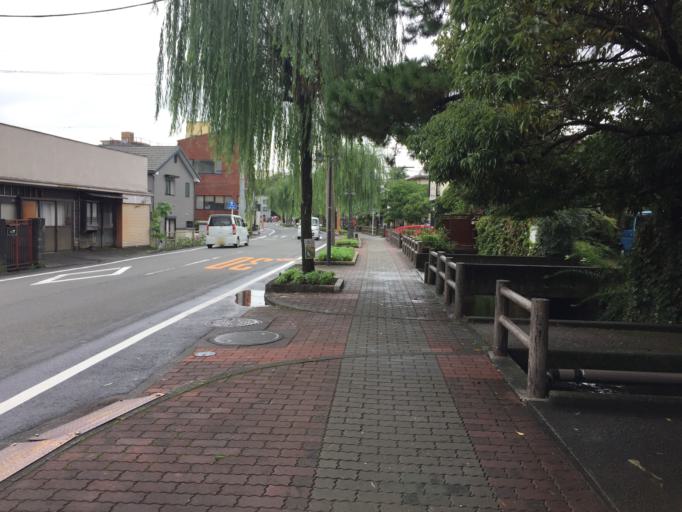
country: JP
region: Shizuoka
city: Mishima
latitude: 35.1215
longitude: 138.9171
